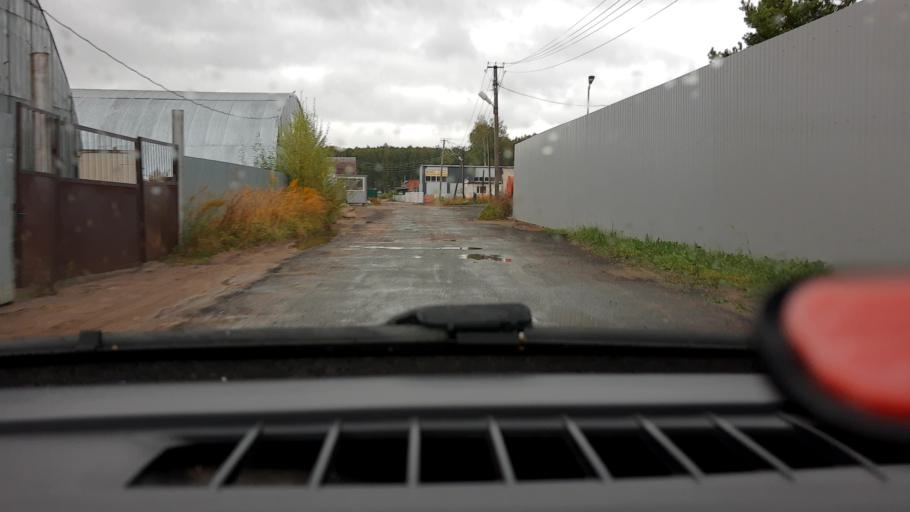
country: RU
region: Nizjnij Novgorod
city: Afonino
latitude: 56.1871
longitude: 44.1212
